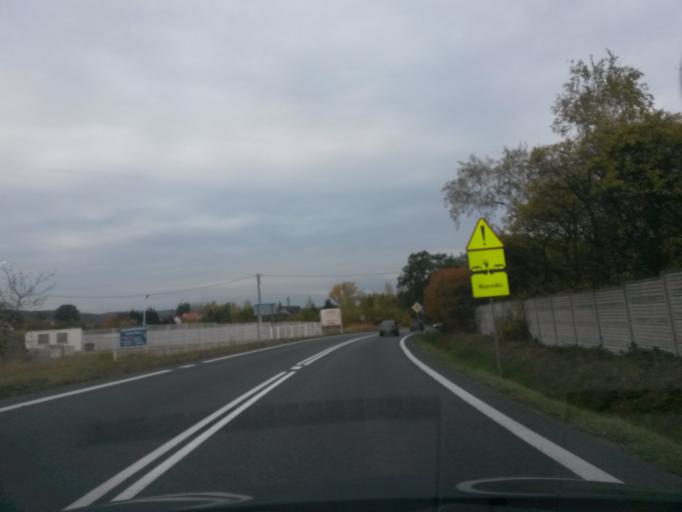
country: PL
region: Lower Silesian Voivodeship
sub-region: Powiat dzierzoniowski
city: Niemcza
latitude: 50.6823
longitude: 16.8206
